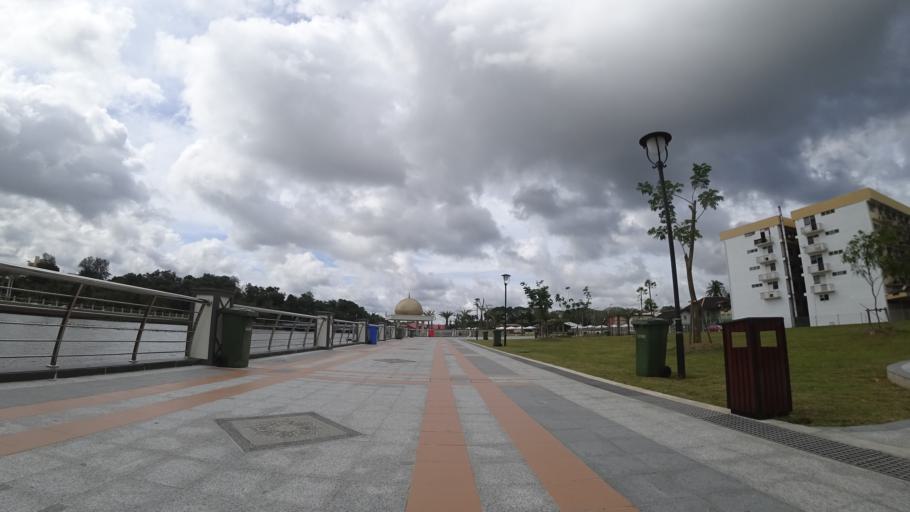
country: BN
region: Brunei and Muara
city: Bandar Seri Begawan
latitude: 4.8910
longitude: 114.9369
